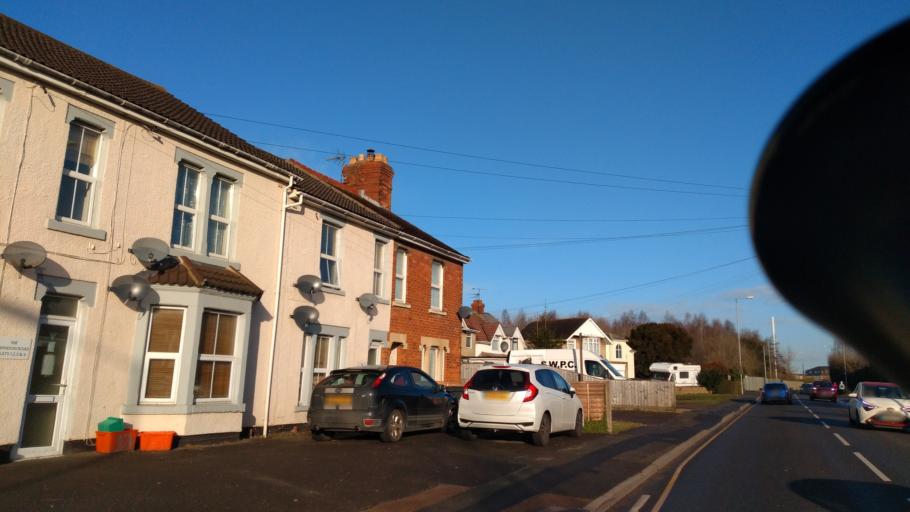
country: GB
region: England
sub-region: Borough of Swindon
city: Swindon
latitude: 51.5779
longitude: -1.7525
